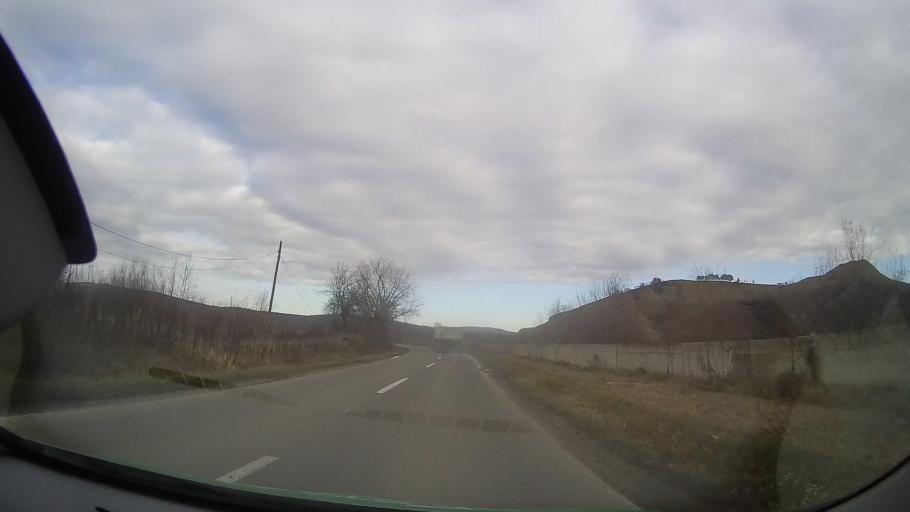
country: RO
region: Mures
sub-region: Comuna Iernut
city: Iernut
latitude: 46.4633
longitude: 24.2179
